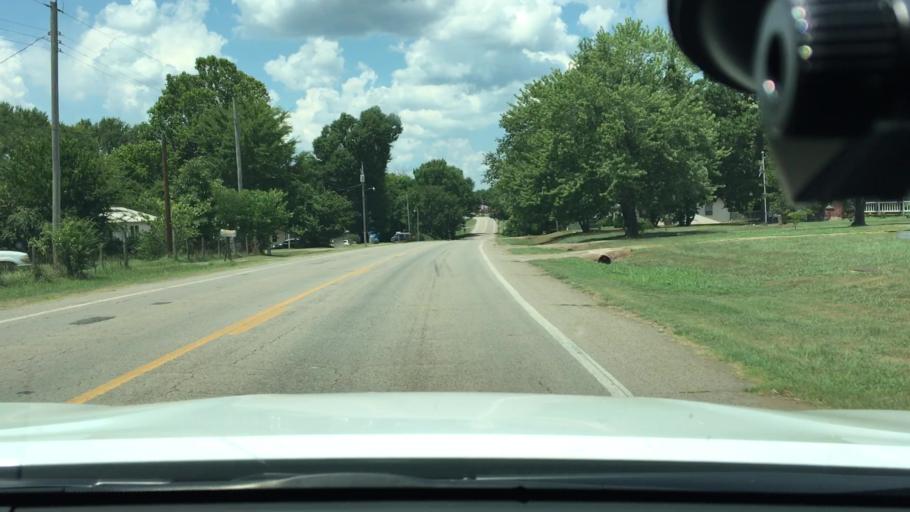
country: US
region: Arkansas
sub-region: Logan County
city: Booneville
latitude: 35.1502
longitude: -93.8163
